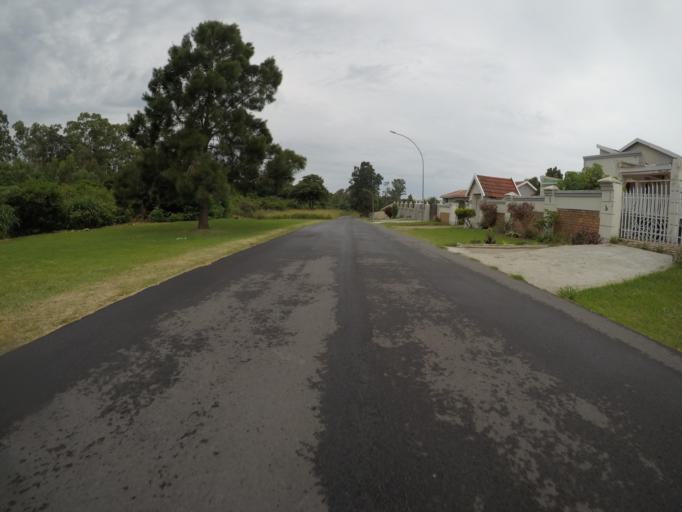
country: ZA
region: Eastern Cape
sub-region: Buffalo City Metropolitan Municipality
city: East London
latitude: -32.9656
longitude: 27.8346
